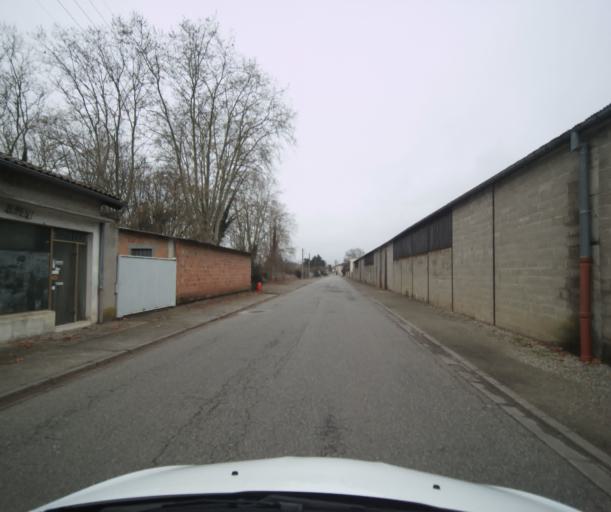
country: FR
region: Midi-Pyrenees
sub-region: Departement du Tarn-et-Garonne
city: Castelsarrasin
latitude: 44.0481
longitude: 1.1120
